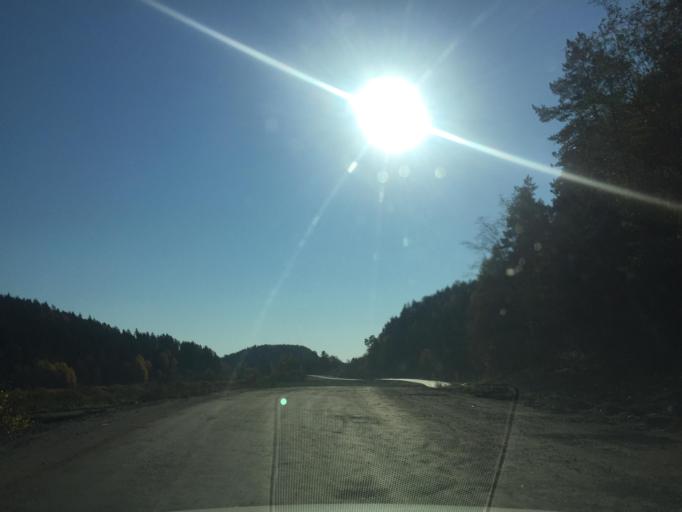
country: RU
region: Leningrad
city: Kuznechnoye
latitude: 61.3222
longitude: 29.8674
